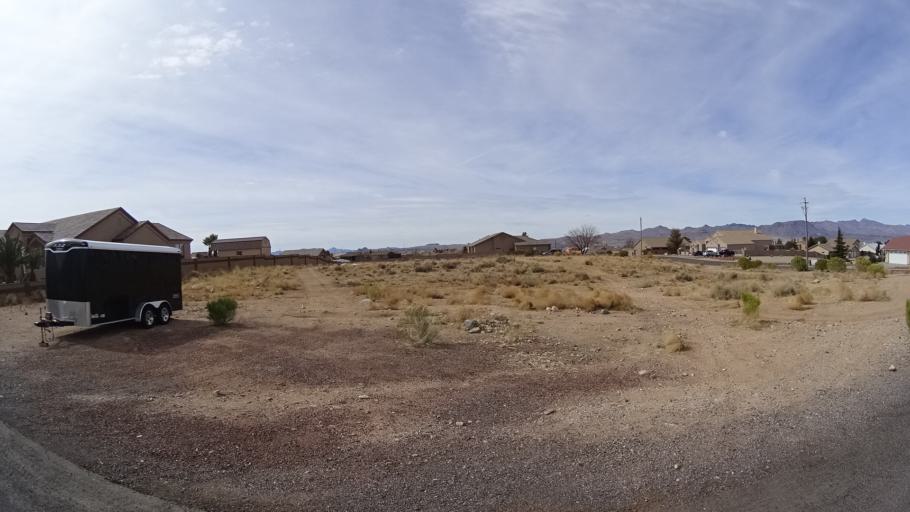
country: US
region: Arizona
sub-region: Mohave County
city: Kingman
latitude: 35.1884
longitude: -113.9763
